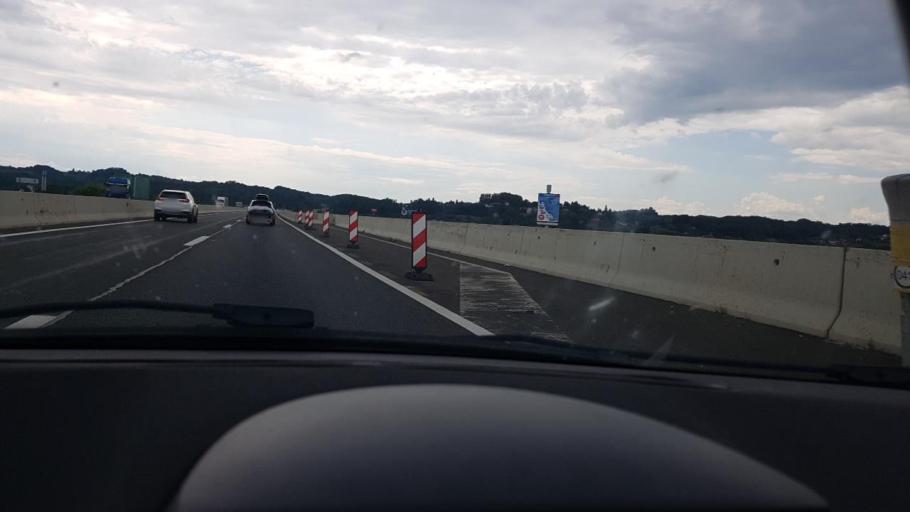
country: HR
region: Karlovacka
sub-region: Grad Karlovac
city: Karlovac
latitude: 45.5115
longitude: 15.5393
